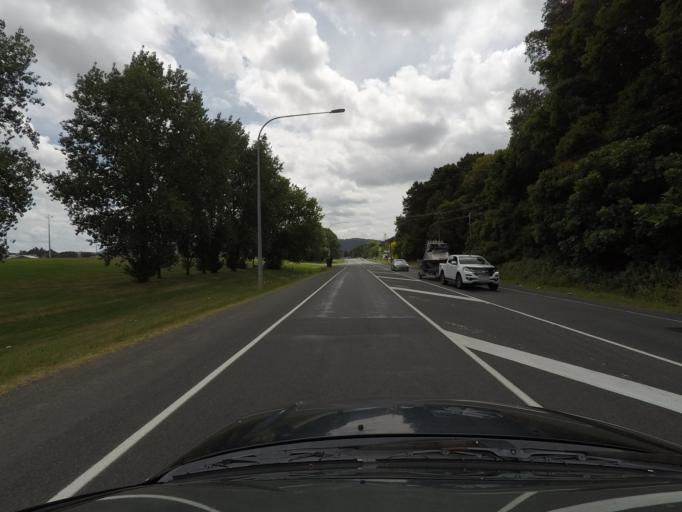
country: NZ
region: Northland
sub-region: Whangarei
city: Whangarei
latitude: -35.7304
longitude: 174.3408
